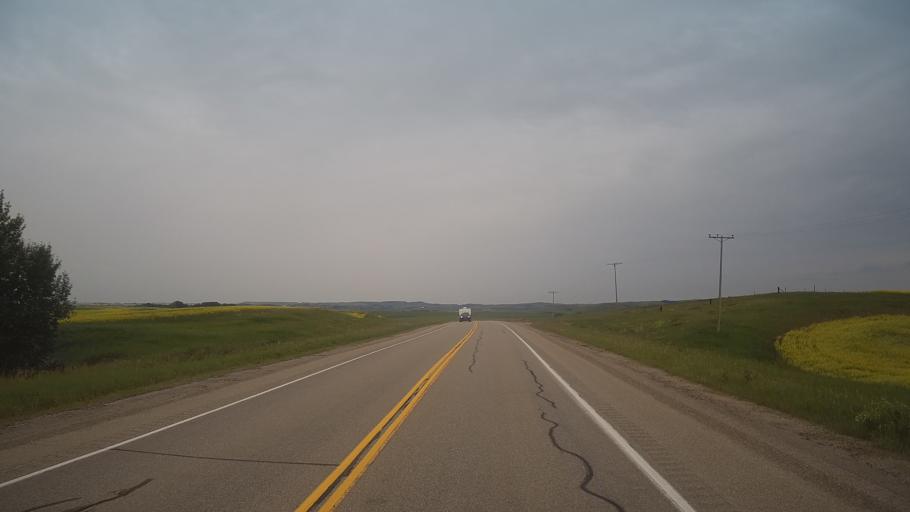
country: CA
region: Saskatchewan
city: Biggar
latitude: 52.0556
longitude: -107.7749
